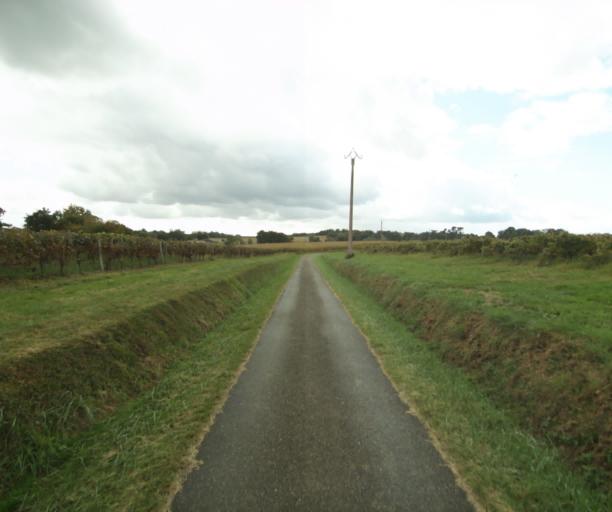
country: FR
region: Midi-Pyrenees
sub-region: Departement du Gers
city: Cazaubon
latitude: 43.8670
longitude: -0.0326
